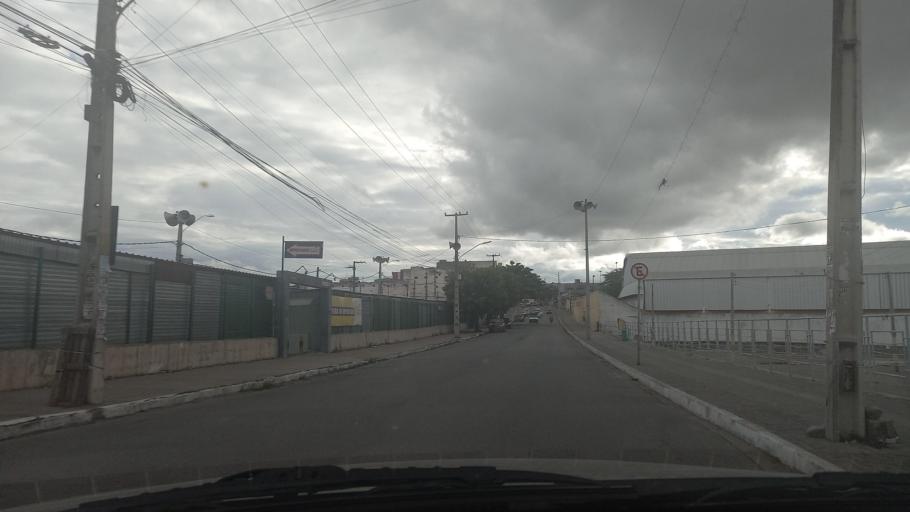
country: BR
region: Pernambuco
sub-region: Caruaru
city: Caruaru
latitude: -8.2928
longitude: -35.9707
